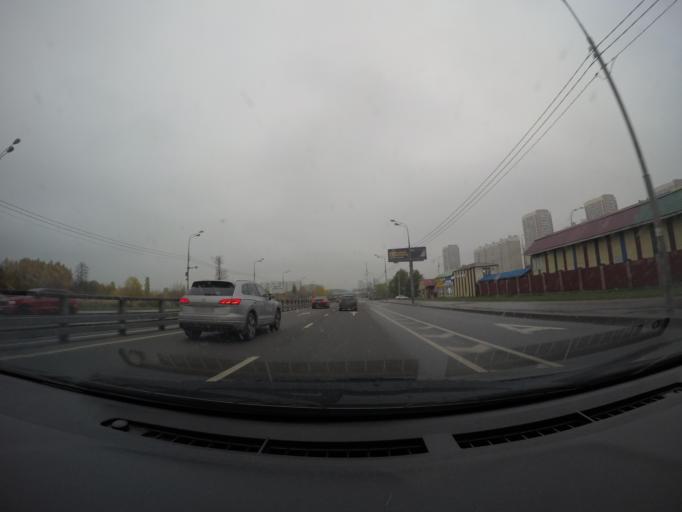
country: RU
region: Moskovskaya
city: Shcherbinka
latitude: 55.5269
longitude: 37.5798
